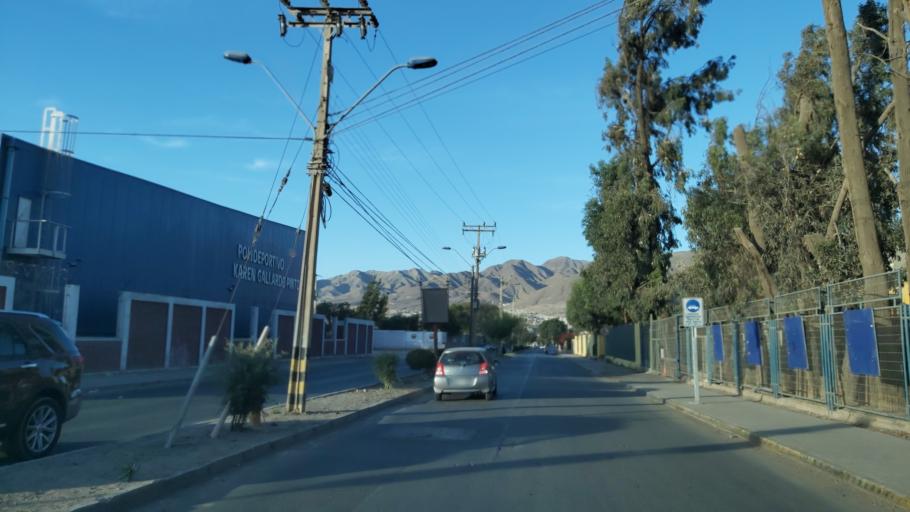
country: CL
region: Atacama
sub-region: Provincia de Copiapo
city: Copiapo
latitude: -27.3788
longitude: -70.3191
